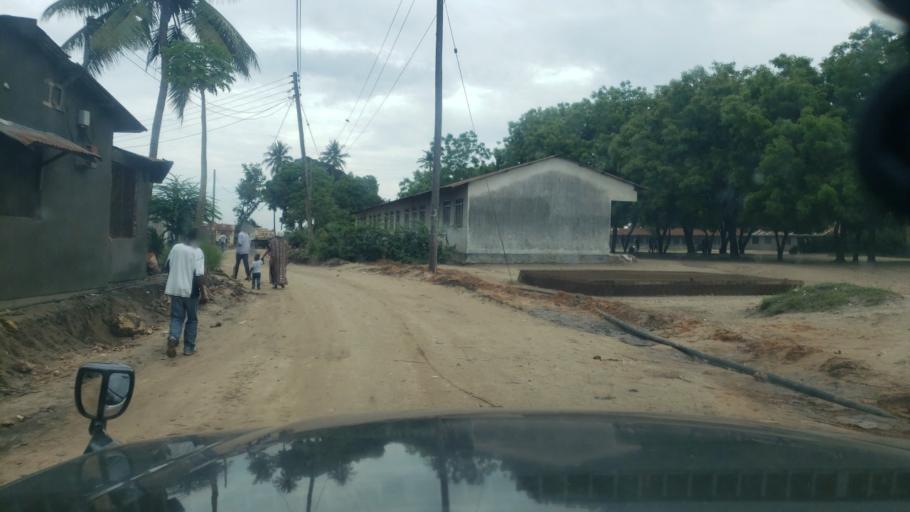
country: TZ
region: Pwani
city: Vikindu
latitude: -6.9245
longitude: 39.2523
